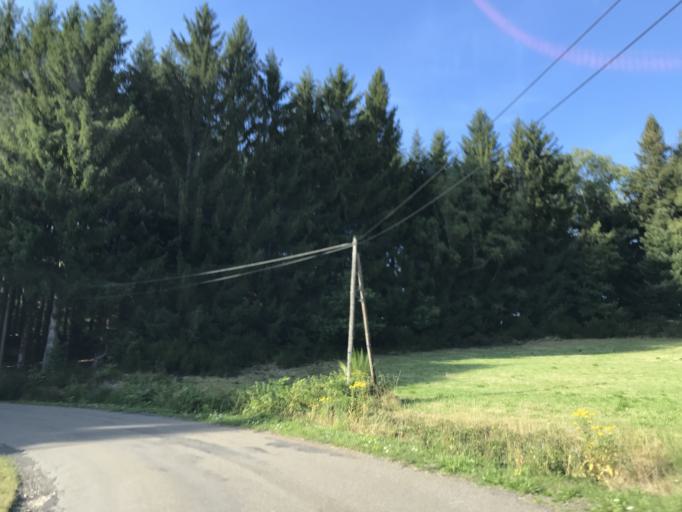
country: FR
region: Auvergne
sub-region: Departement du Puy-de-Dome
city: Job
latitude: 45.6778
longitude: 3.7318
